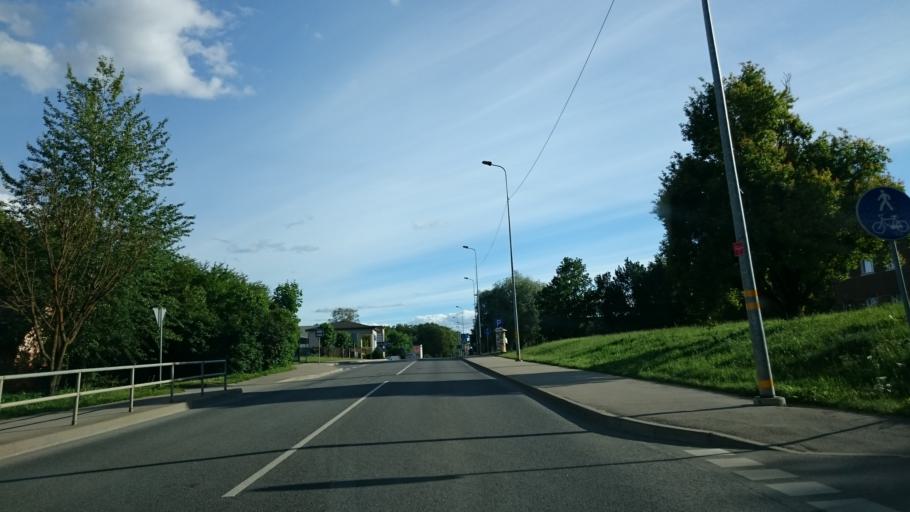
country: LV
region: Saldus Rajons
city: Saldus
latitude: 56.6614
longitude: 22.4762
